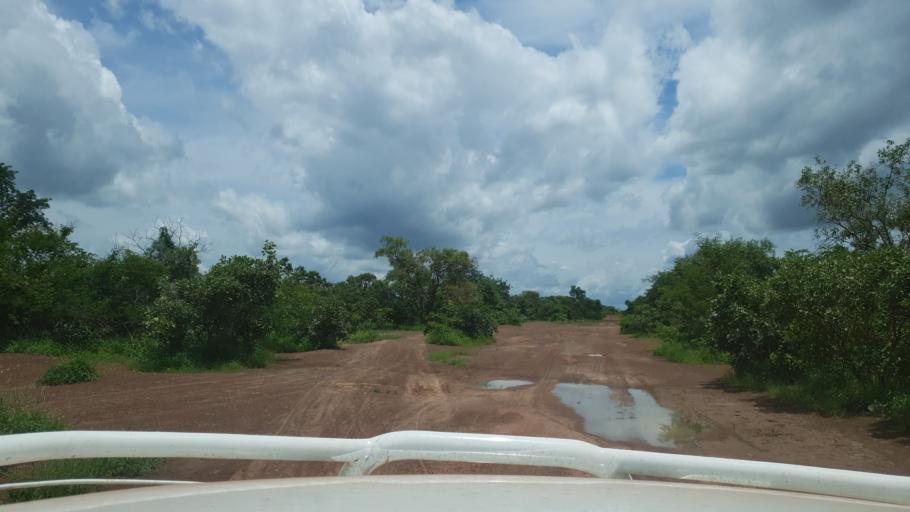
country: ML
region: Koulikoro
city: Banamba
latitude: 13.1973
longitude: -7.3254
